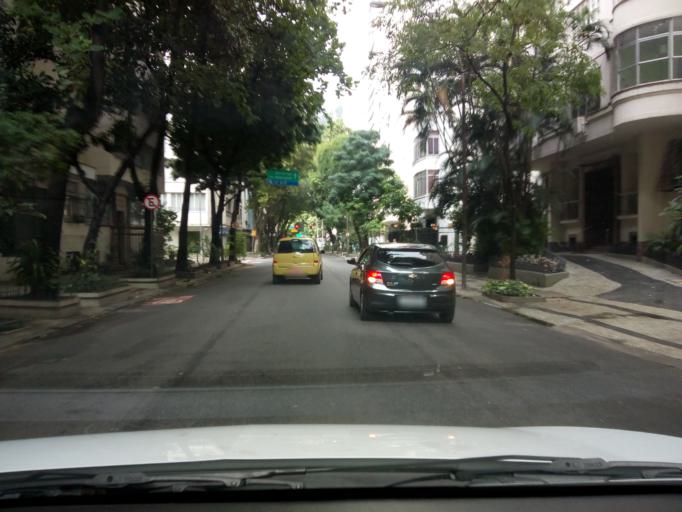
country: BR
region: Rio de Janeiro
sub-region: Rio De Janeiro
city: Rio de Janeiro
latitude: -22.9664
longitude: -43.1846
